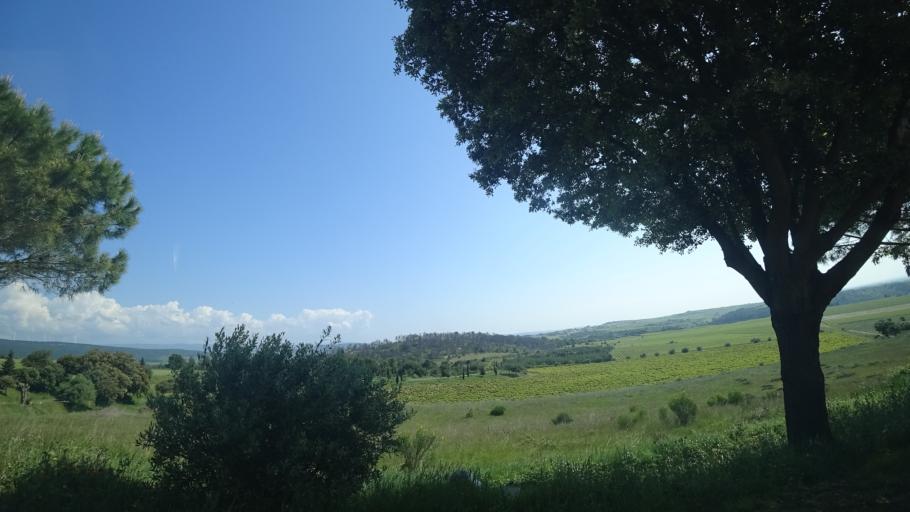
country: FR
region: Languedoc-Roussillon
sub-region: Departement de l'Aude
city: Canet
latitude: 43.2591
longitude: 2.8165
